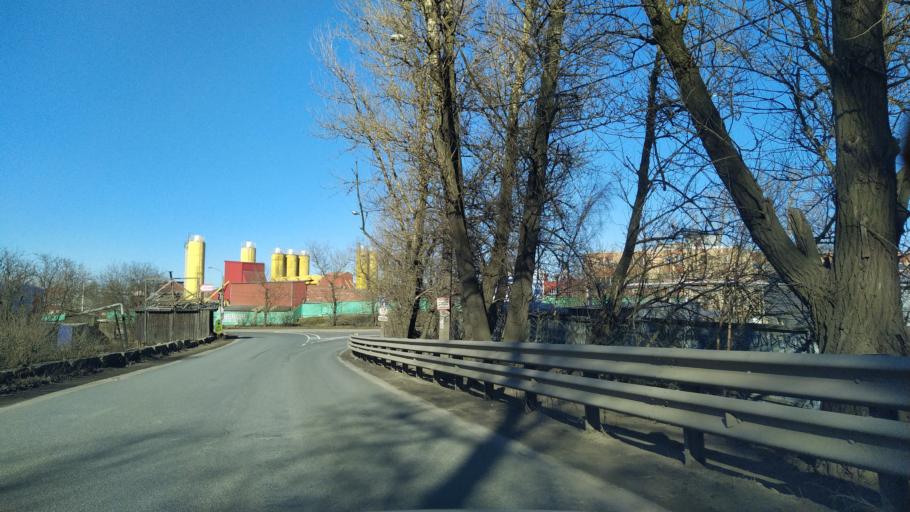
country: RU
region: St.-Petersburg
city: Centralniy
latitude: 59.9055
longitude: 30.3786
